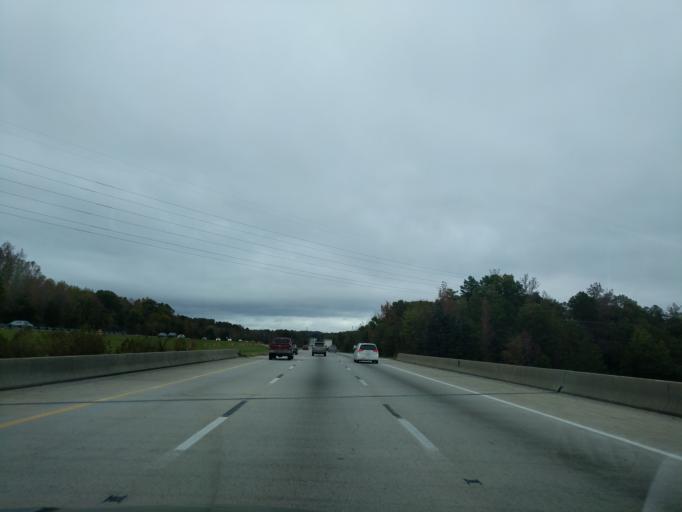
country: US
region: North Carolina
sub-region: Guilford County
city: Jamestown
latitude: 35.9617
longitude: -79.8941
